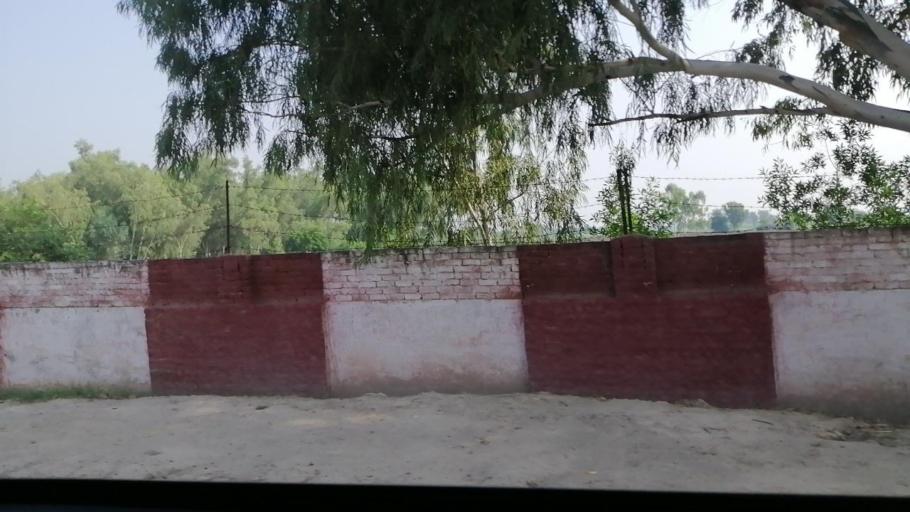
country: PK
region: Punjab
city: Kamalia
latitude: 30.7139
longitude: 72.6806
